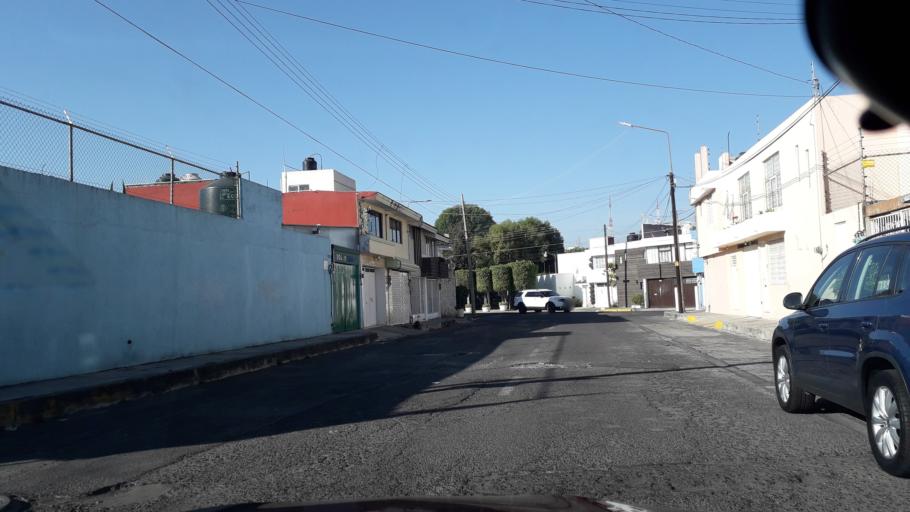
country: MX
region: Puebla
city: Puebla
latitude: 19.0629
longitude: -98.2199
